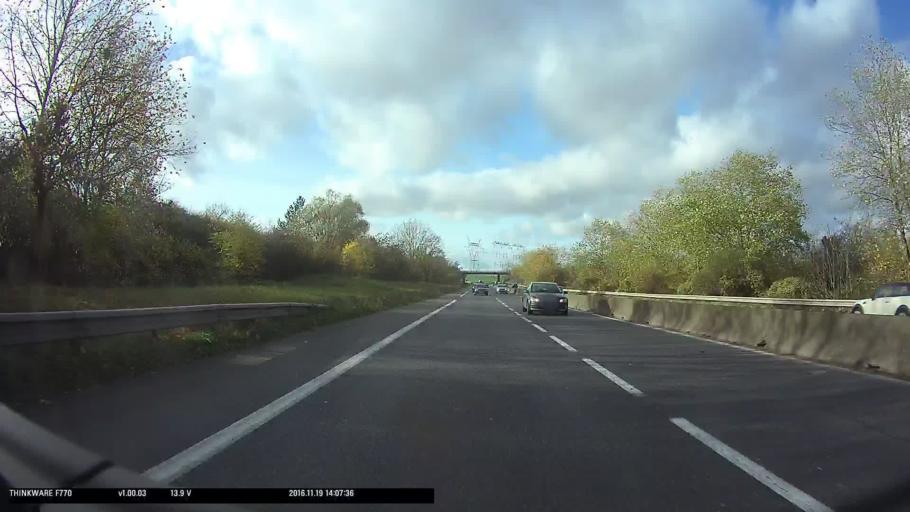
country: FR
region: Ile-de-France
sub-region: Departement du Val-d'Oise
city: Vaureal
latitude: 49.0599
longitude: 2.0237
